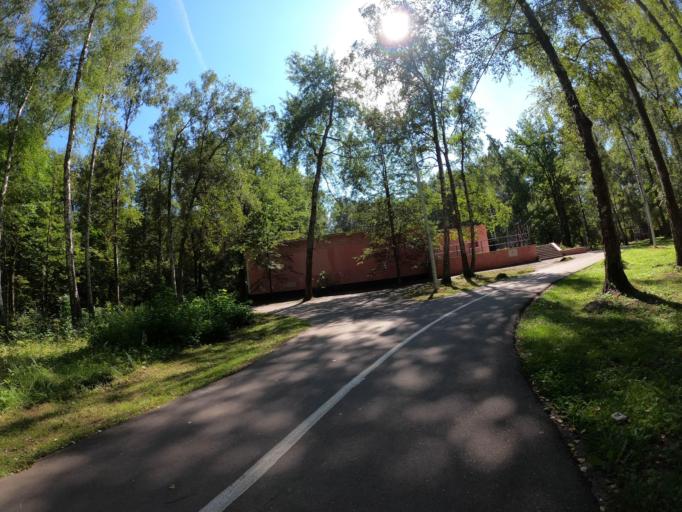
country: RU
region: Moskovskaya
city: Stupino
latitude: 54.8813
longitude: 38.0893
